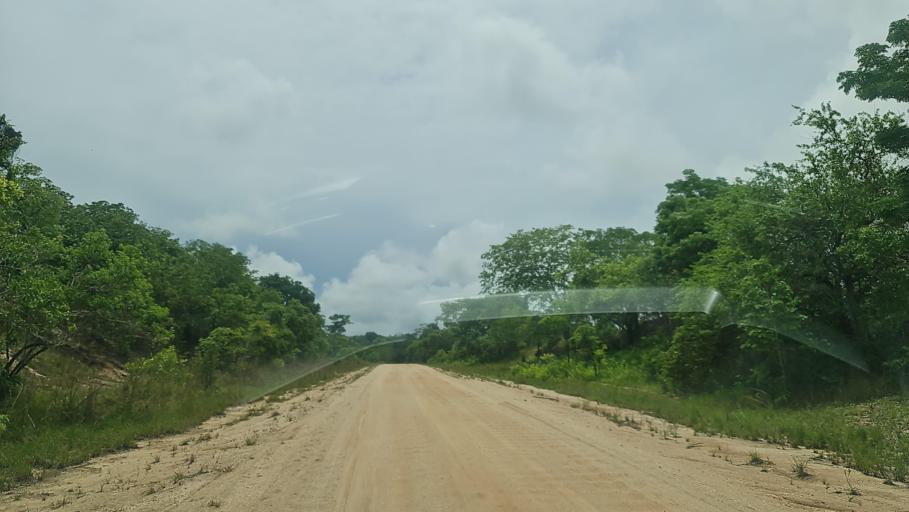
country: MZ
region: Zambezia
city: Quelimane
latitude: -17.2701
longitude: 37.2562
